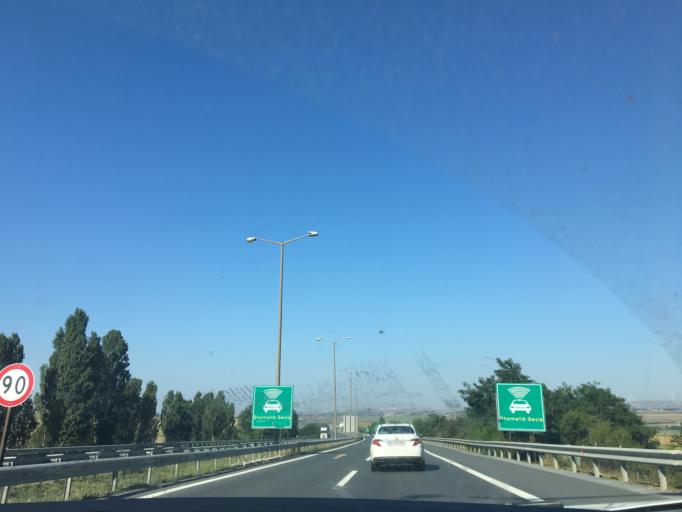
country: TR
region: Istanbul
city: Silivri
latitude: 41.1156
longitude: 28.1764
